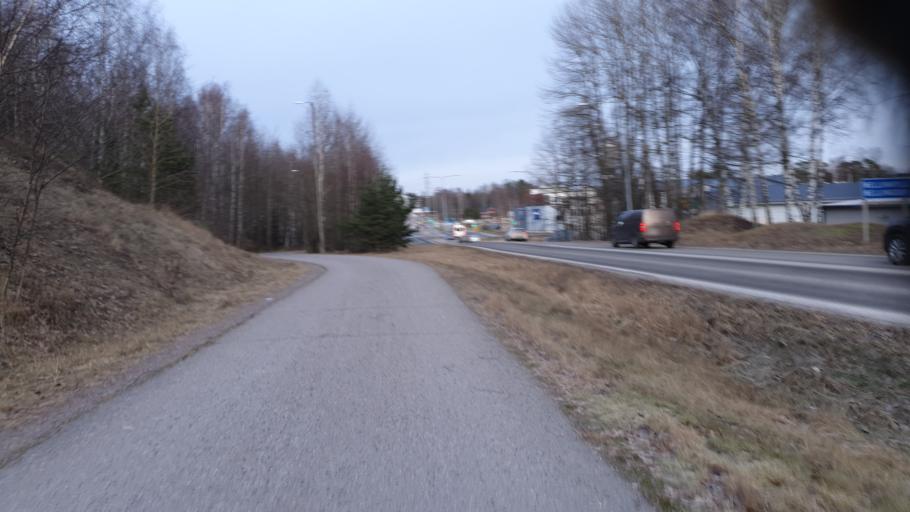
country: FI
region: Uusimaa
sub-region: Helsinki
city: Vantaa
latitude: 60.2262
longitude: 25.1190
